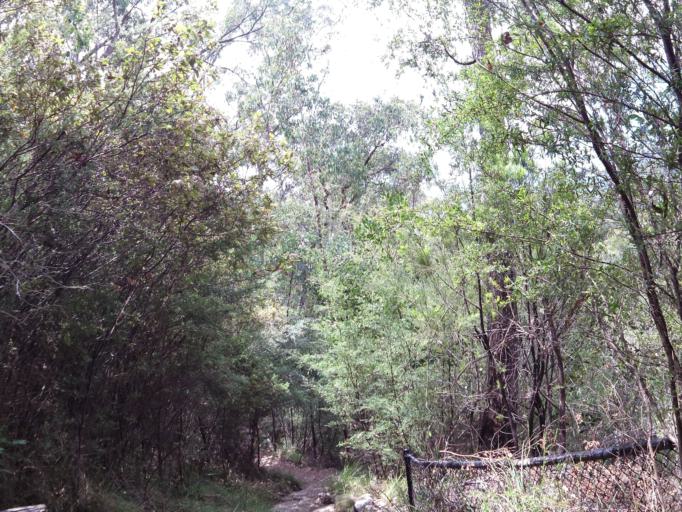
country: AU
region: Victoria
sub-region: Alpine
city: Mount Beauty
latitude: -36.7180
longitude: 146.8381
